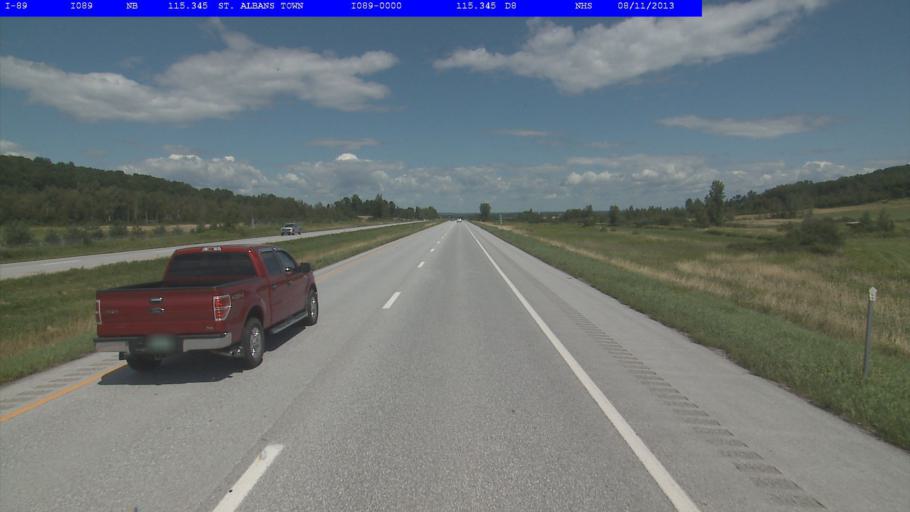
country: US
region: Vermont
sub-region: Franklin County
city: Saint Albans
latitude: 44.8173
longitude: -73.0631
